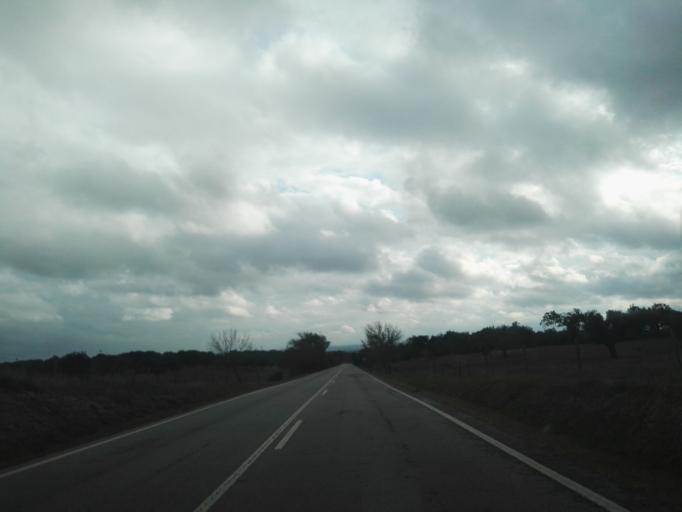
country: PT
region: Portalegre
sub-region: Arronches
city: Arronches
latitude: 39.0788
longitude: -7.2801
